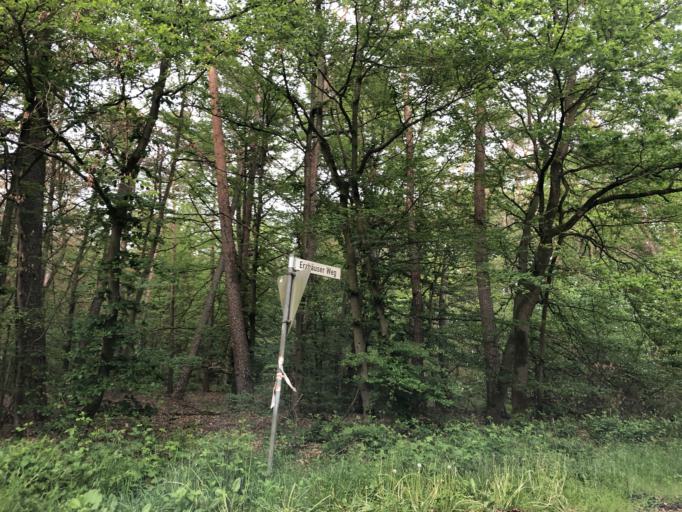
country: DE
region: Hesse
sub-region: Regierungsbezirk Darmstadt
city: Erzhausen
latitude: 49.9473
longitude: 8.6051
